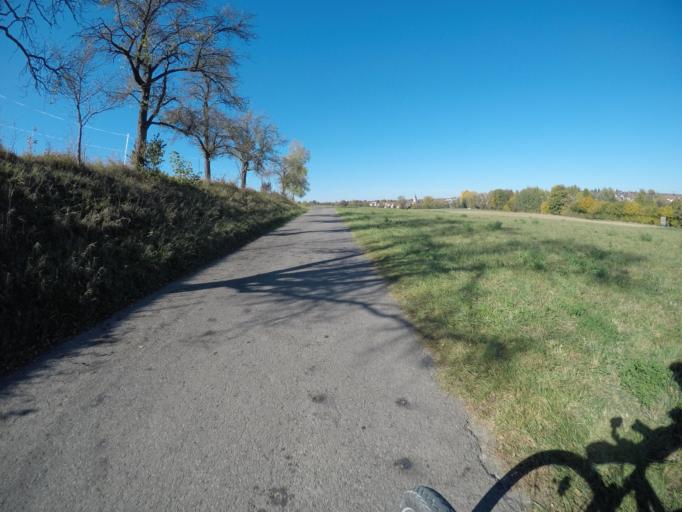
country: DE
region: Baden-Wuerttemberg
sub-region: Tuebingen Region
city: Rottenburg
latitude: 48.5298
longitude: 8.9543
